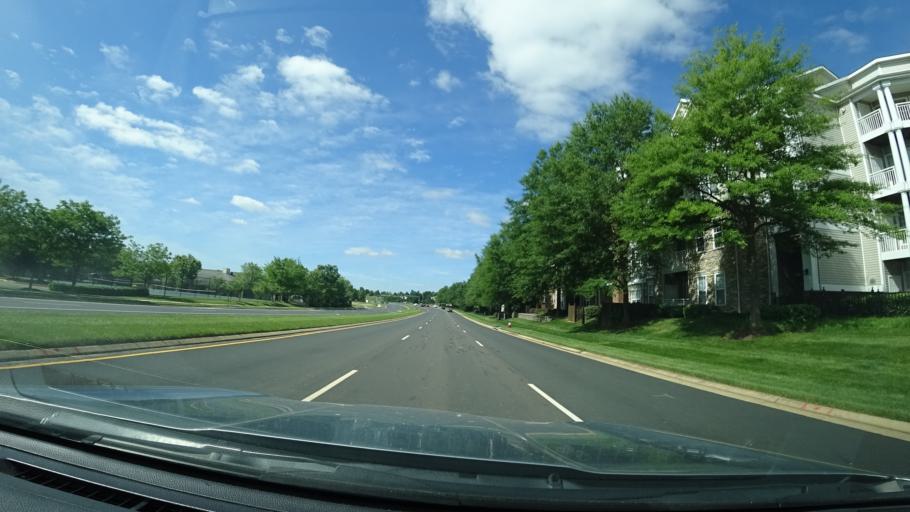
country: US
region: Virginia
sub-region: Loudoun County
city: Dulles Town Center
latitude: 39.0352
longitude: -77.4169
